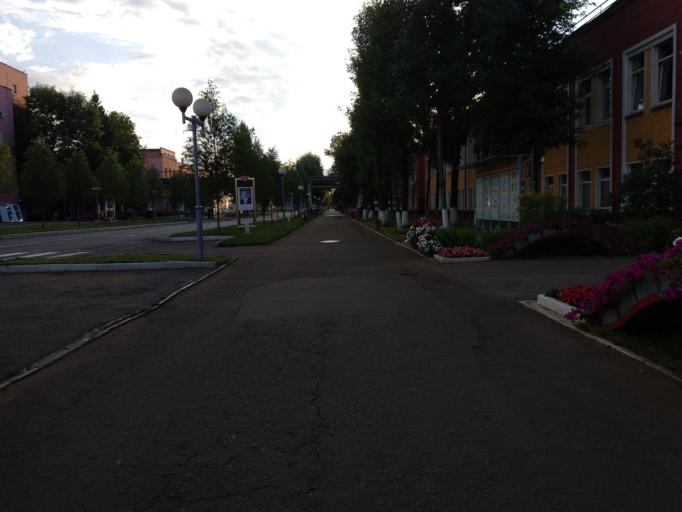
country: BY
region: Minsk
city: Minsk
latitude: 53.8913
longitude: 27.6203
